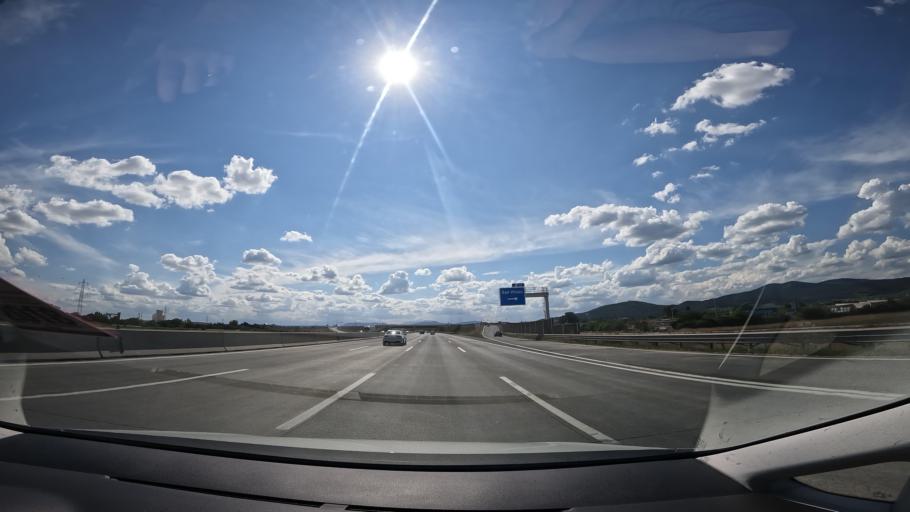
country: AT
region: Lower Austria
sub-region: Politischer Bezirk Baden
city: Gunselsdorf
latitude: 47.9686
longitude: 16.2515
